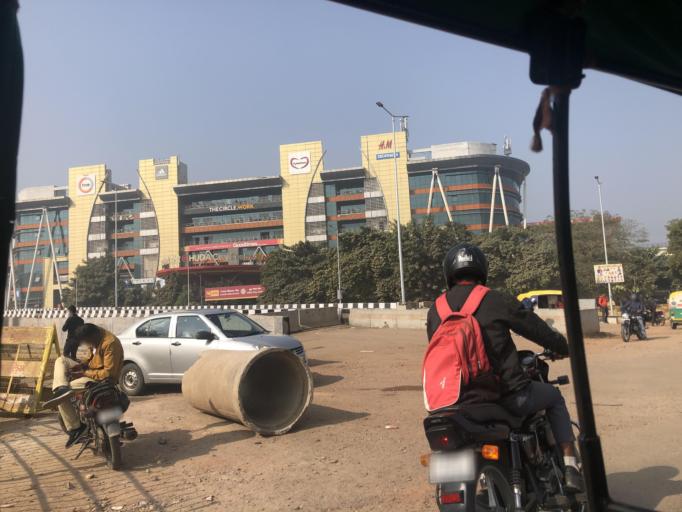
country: IN
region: Haryana
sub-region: Gurgaon
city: Gurgaon
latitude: 28.4586
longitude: 77.0740
